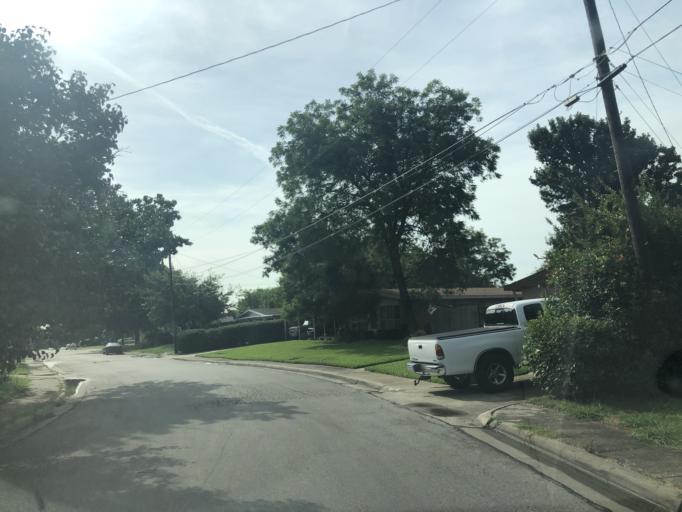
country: US
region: Texas
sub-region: Dallas County
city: Irving
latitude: 32.8035
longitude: -96.9673
